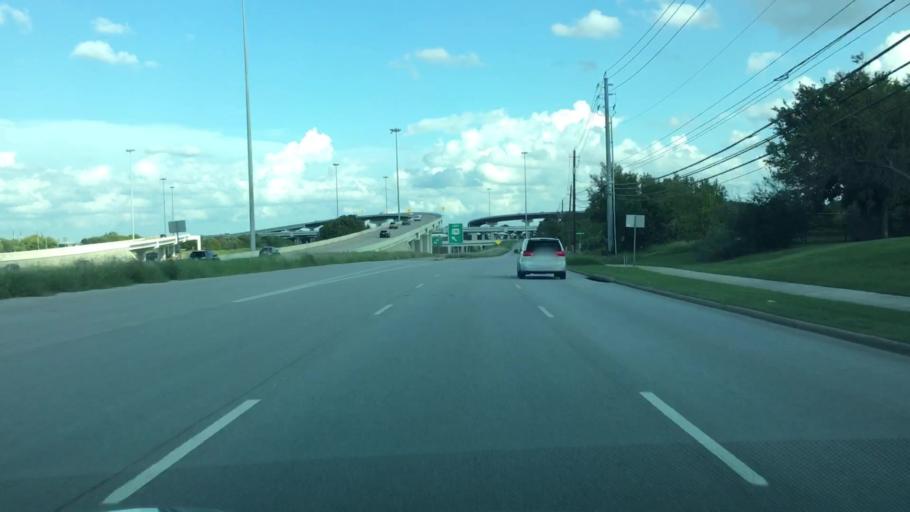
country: US
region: Texas
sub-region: Travis County
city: Rollingwood
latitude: 30.2360
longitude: -97.8301
